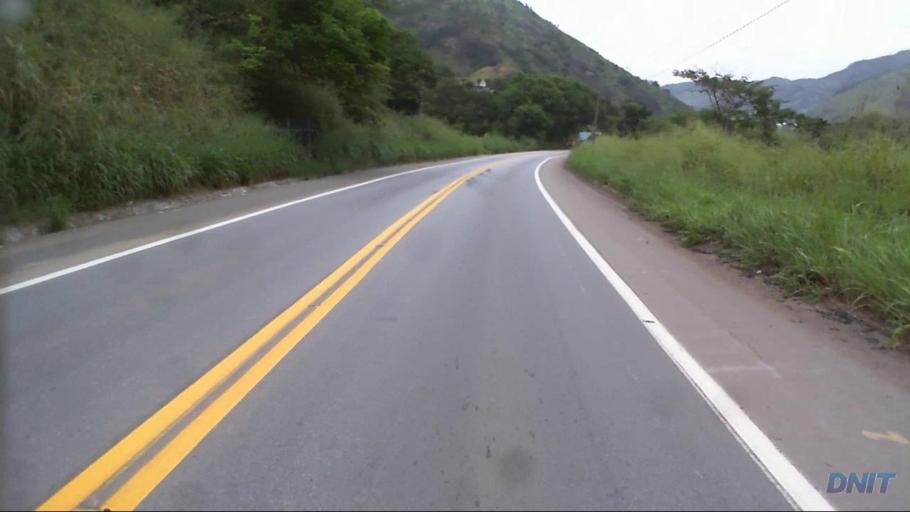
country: BR
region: Minas Gerais
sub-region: Timoteo
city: Timoteo
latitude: -19.5578
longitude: -42.7102
